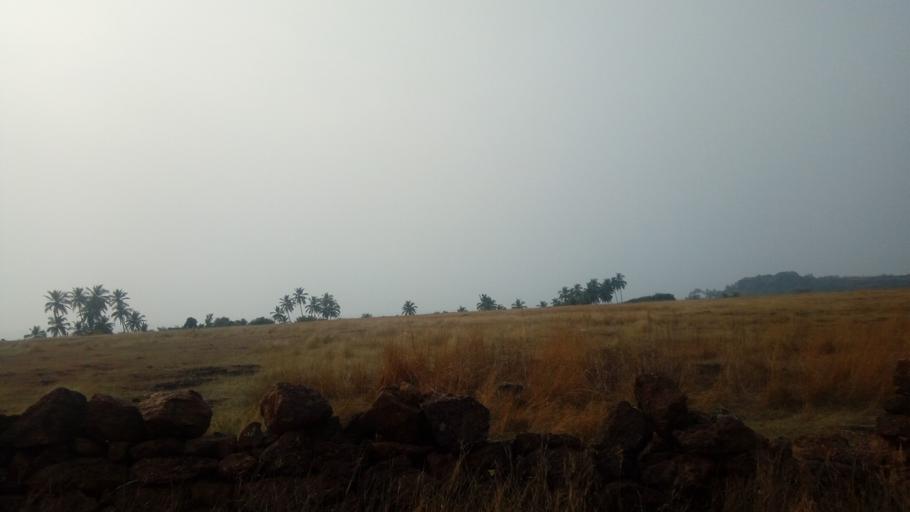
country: IN
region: Goa
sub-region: South Goa
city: Cavelossim
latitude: 15.0993
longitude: 73.9287
